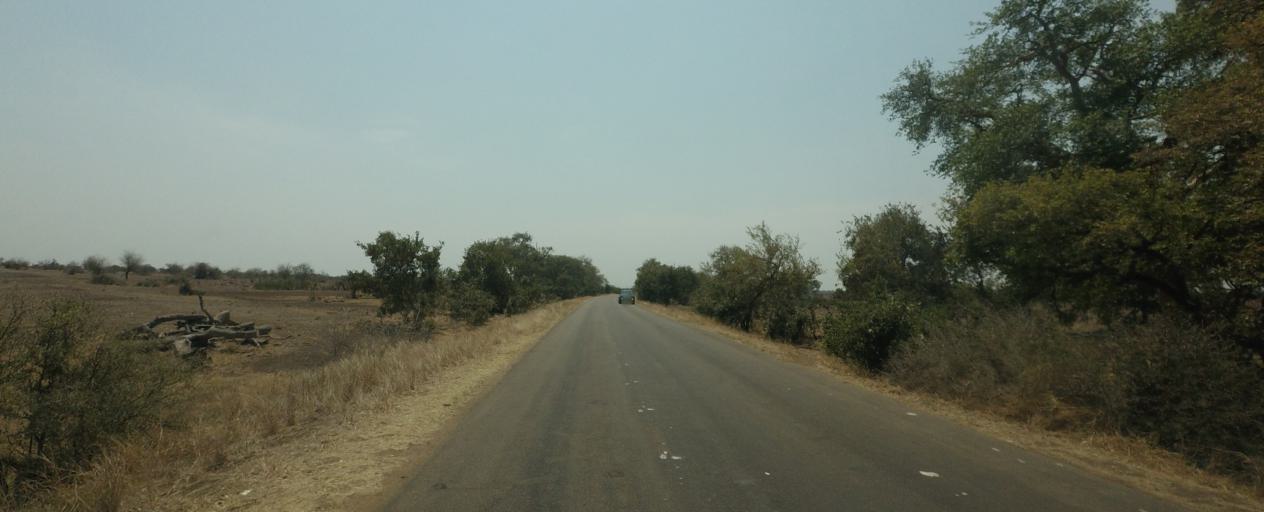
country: ZA
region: Limpopo
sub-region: Mopani District Municipality
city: Phalaborwa
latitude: -24.1619
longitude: 31.7201
